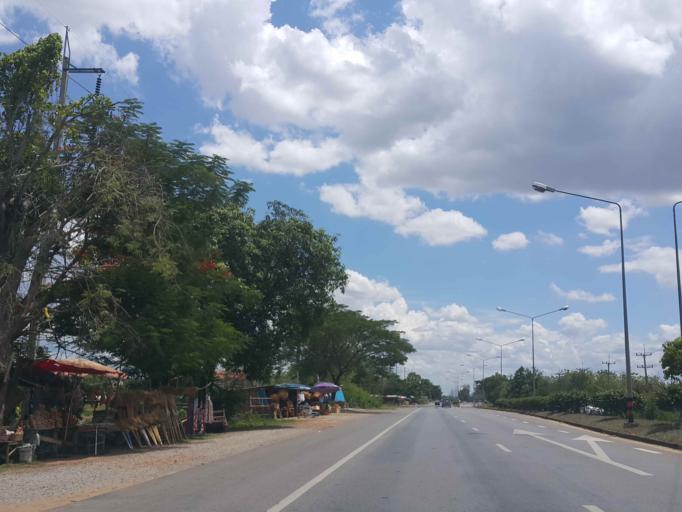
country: TH
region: Phrae
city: Nong Muang Khai
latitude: 18.2506
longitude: 100.2275
